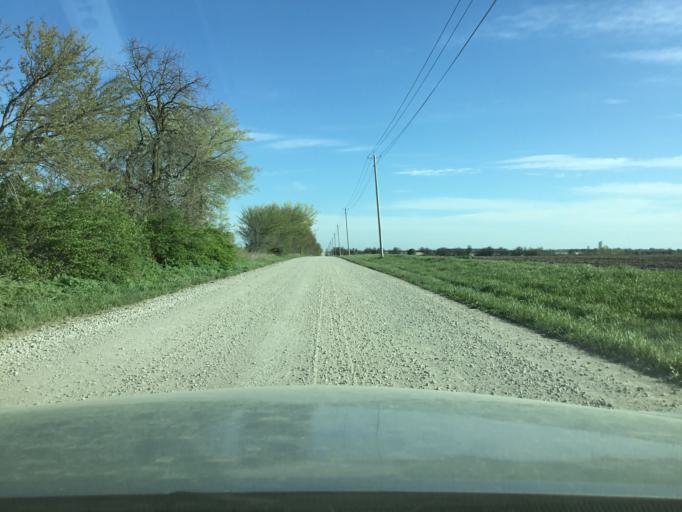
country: US
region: Kansas
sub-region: Neosho County
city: Chanute
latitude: 37.6473
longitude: -95.4893
